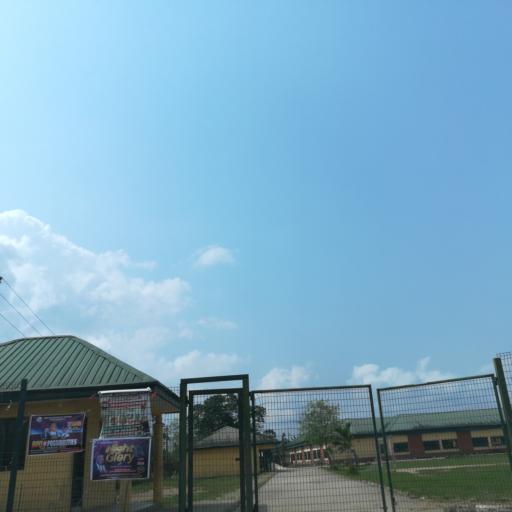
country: NG
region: Rivers
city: Okrika
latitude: 4.7943
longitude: 7.1146
